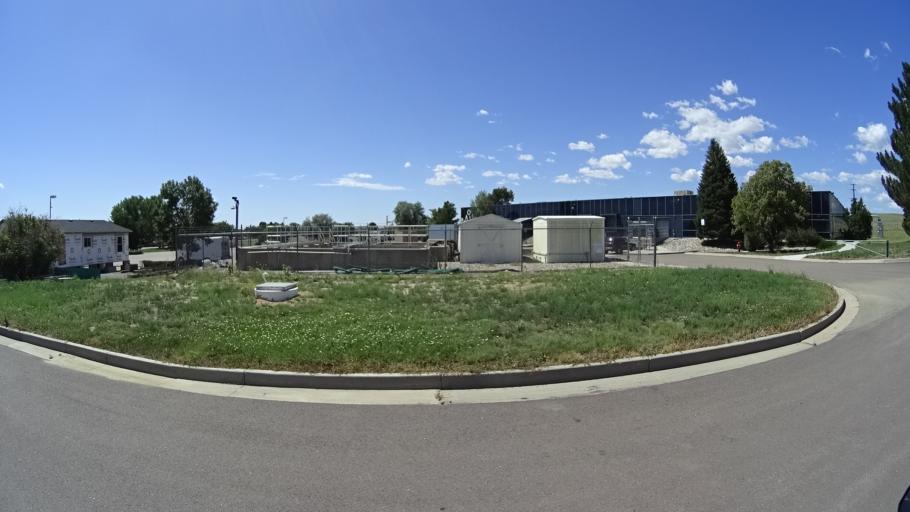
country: US
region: Colorado
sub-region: El Paso County
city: Security-Widefield
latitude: 38.7678
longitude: -104.6703
